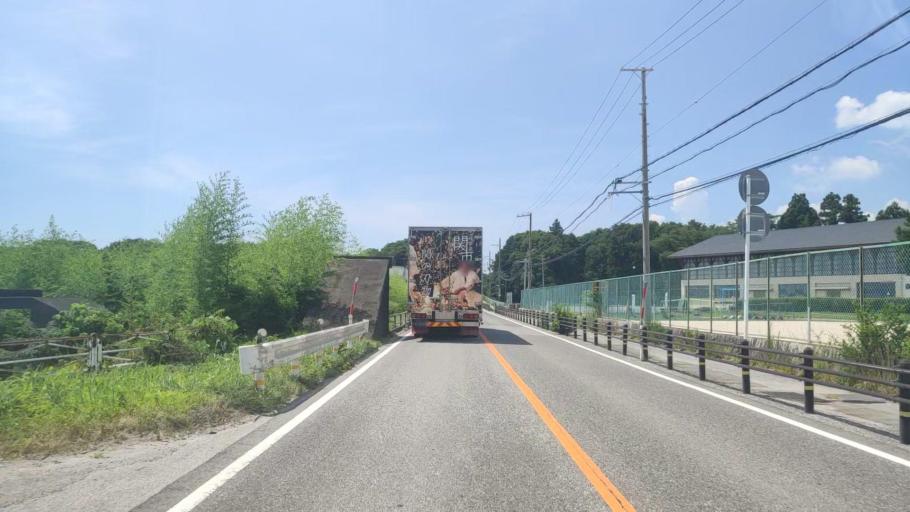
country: JP
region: Shiga Prefecture
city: Nagahama
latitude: 35.3738
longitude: 136.3861
